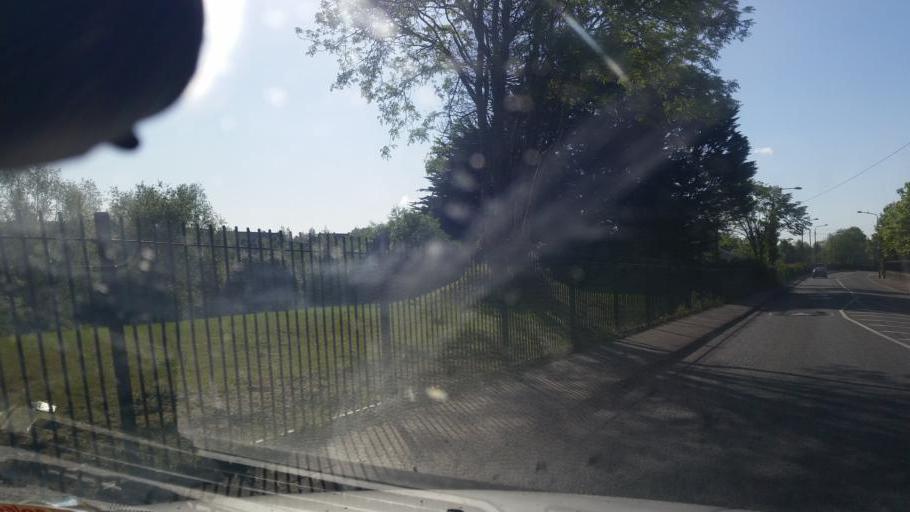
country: IE
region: Leinster
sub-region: Fingal County
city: Blanchardstown
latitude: 53.4018
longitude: -6.3957
